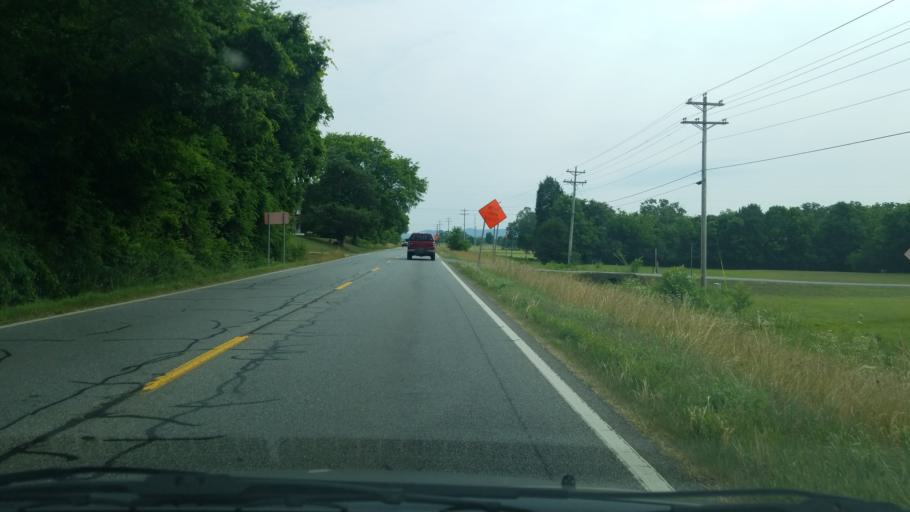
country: US
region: Georgia
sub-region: Catoosa County
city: Ringgold
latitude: 34.8872
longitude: -85.1354
